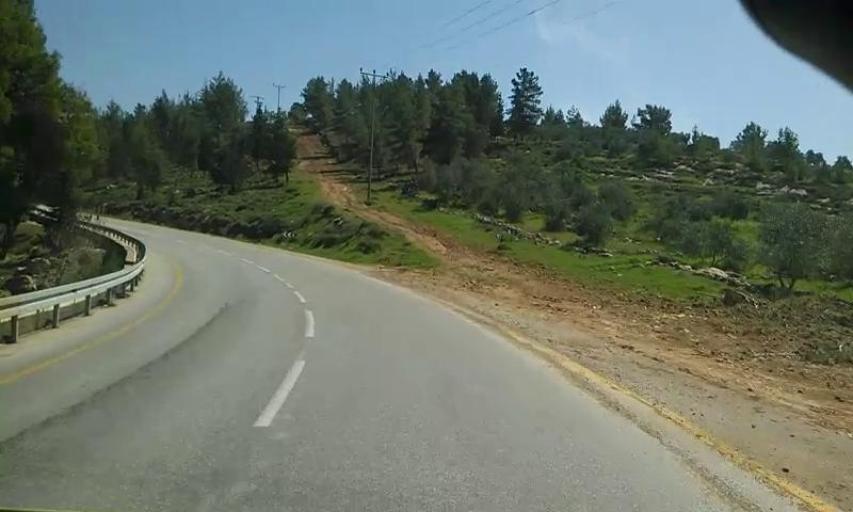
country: PS
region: West Bank
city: Nahhalin
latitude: 31.6736
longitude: 35.1013
